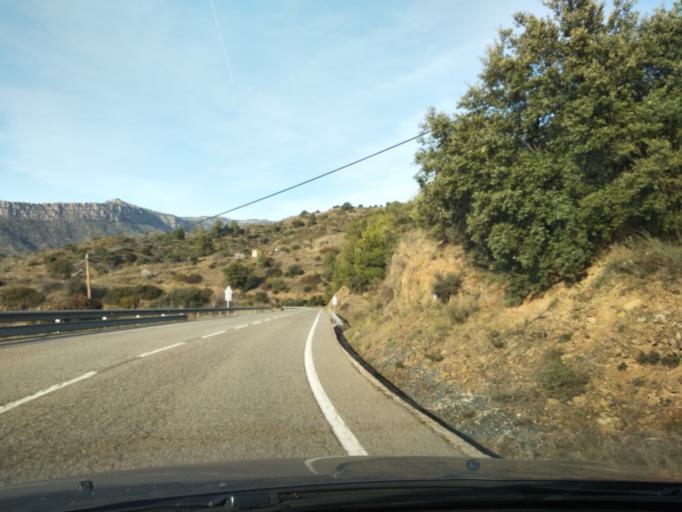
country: ES
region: Catalonia
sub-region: Provincia de Tarragona
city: Margalef
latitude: 41.2101
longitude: 0.7721
